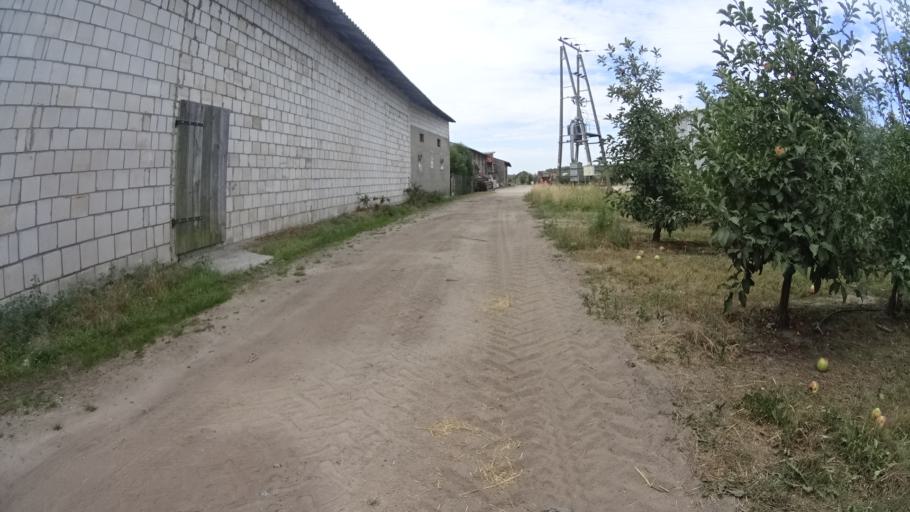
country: PL
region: Masovian Voivodeship
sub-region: Powiat bialobrzeski
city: Wysmierzyce
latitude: 51.6519
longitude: 20.7988
